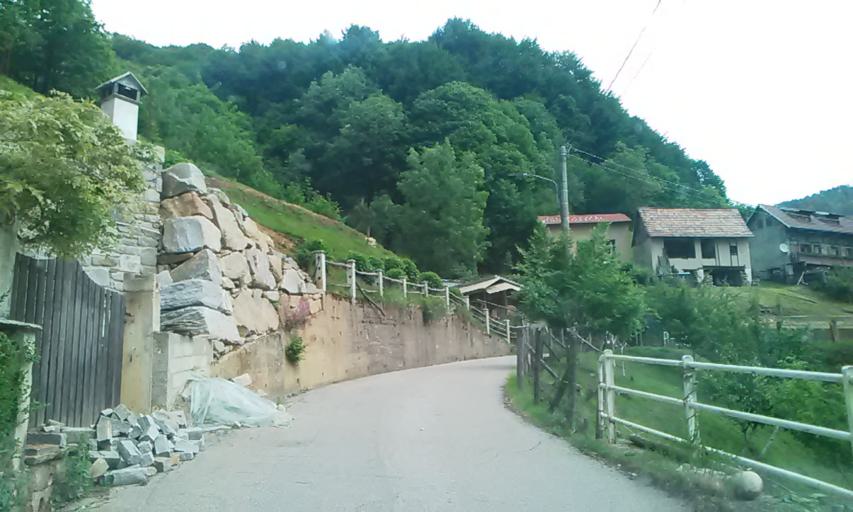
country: IT
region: Piedmont
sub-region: Provincia di Vercelli
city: Civiasco
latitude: 45.8161
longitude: 8.3111
